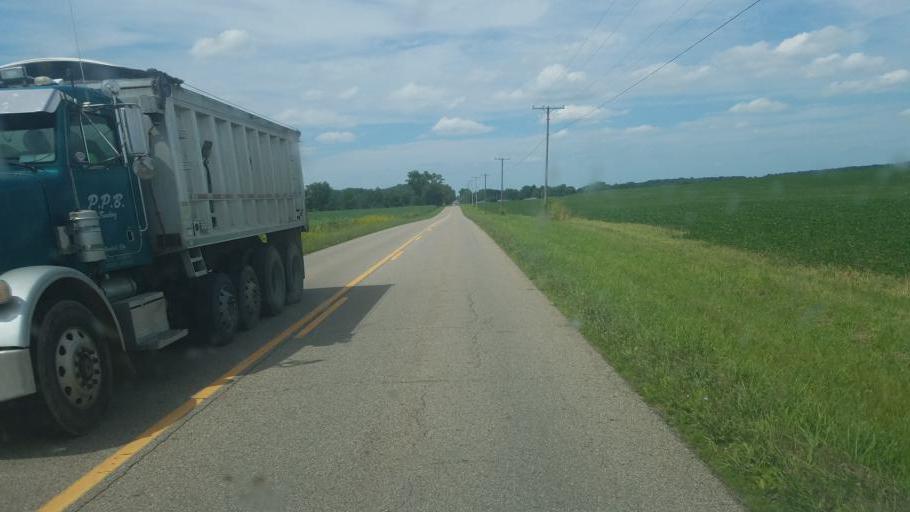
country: US
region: Ohio
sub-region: Knox County
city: Fredericktown
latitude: 40.4598
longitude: -82.5417
